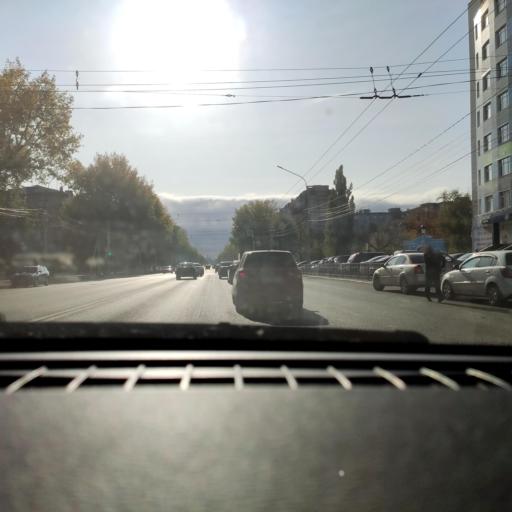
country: RU
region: Voronezj
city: Voronezh
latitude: 51.6473
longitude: 39.2396
